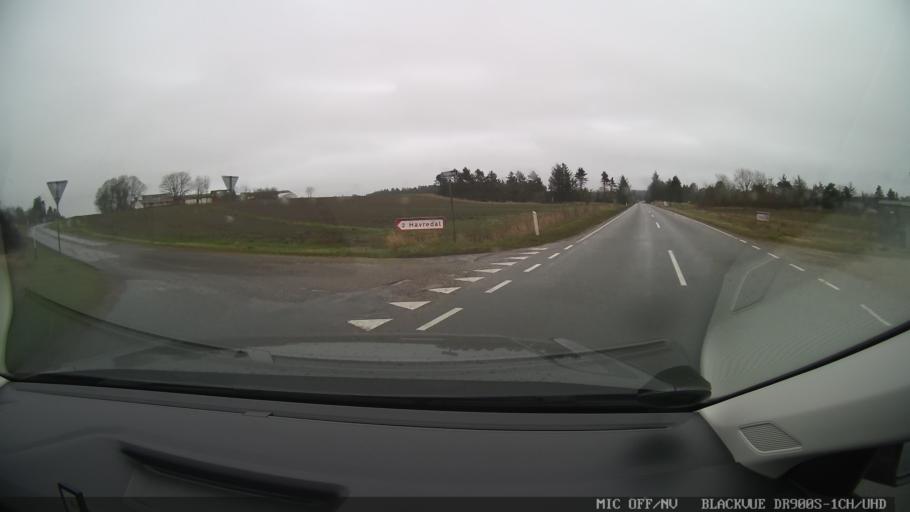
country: DK
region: Central Jutland
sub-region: Viborg Kommune
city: Karup
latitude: 56.3061
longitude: 9.2378
